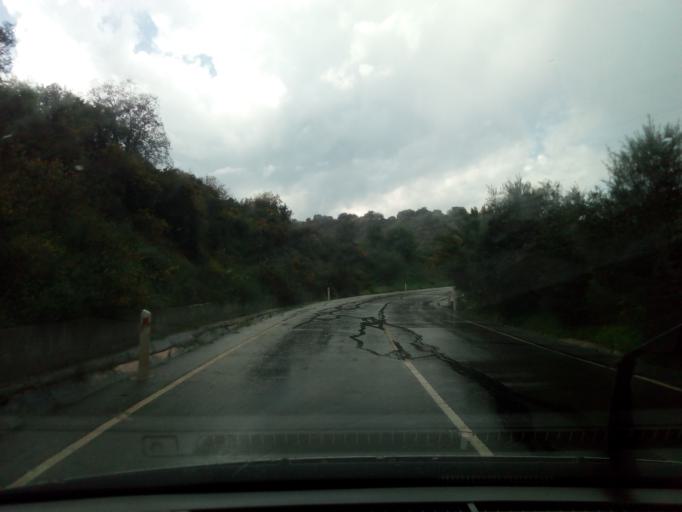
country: CY
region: Pafos
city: Polis
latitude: 35.0046
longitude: 32.4621
